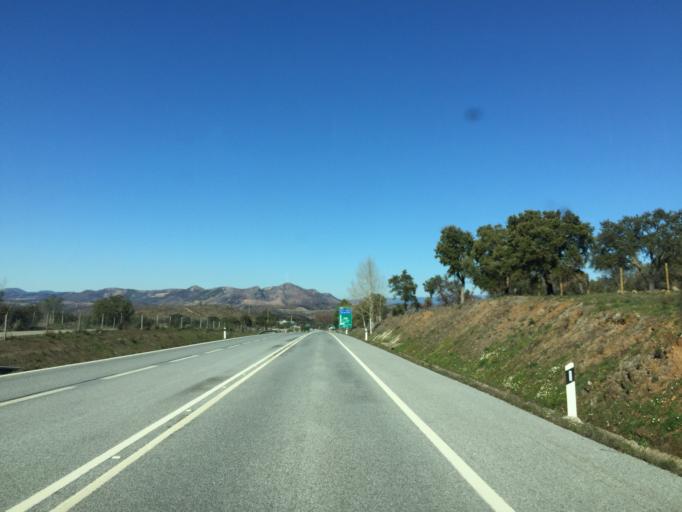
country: PT
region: Portalegre
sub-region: Nisa
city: Nisa
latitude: 39.5265
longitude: -7.7851
